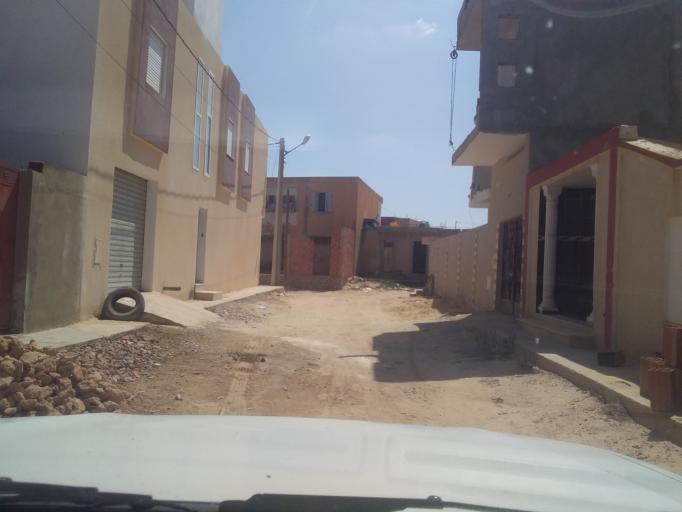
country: TN
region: Qabis
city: Matmata
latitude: 33.6159
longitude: 10.2860
